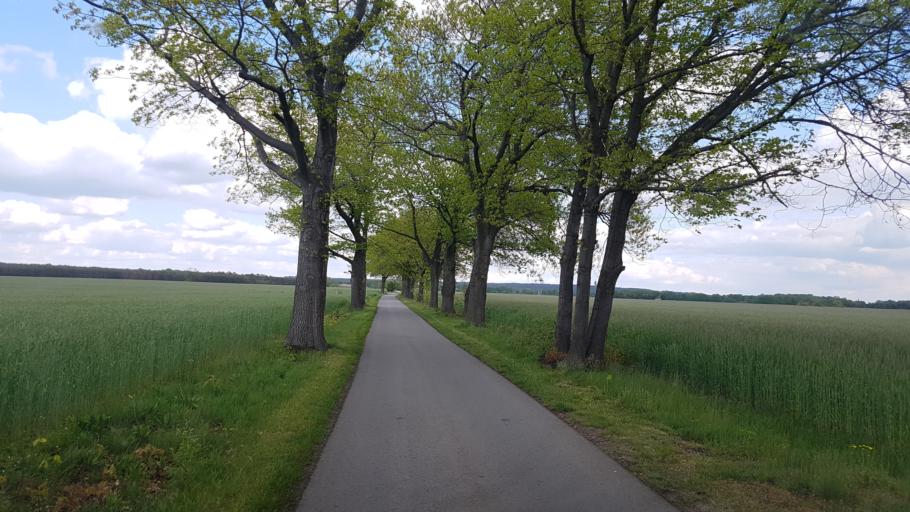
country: DE
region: Saxony
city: Nauwalde
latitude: 51.4664
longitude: 13.4374
